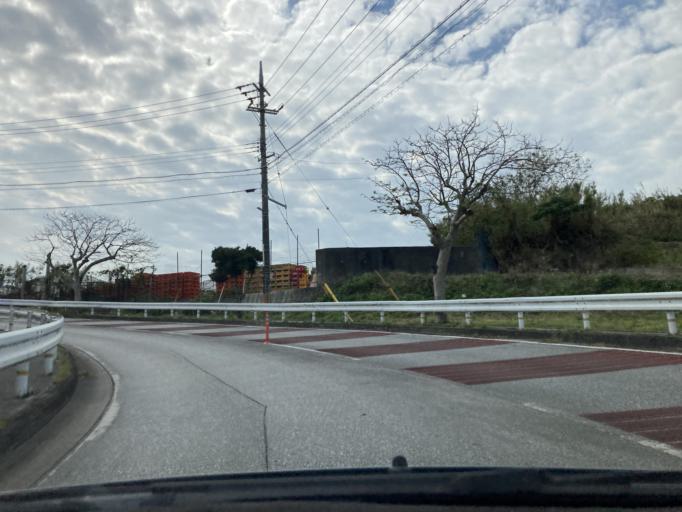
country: JP
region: Okinawa
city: Tomigusuku
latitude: 26.1835
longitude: 127.6941
